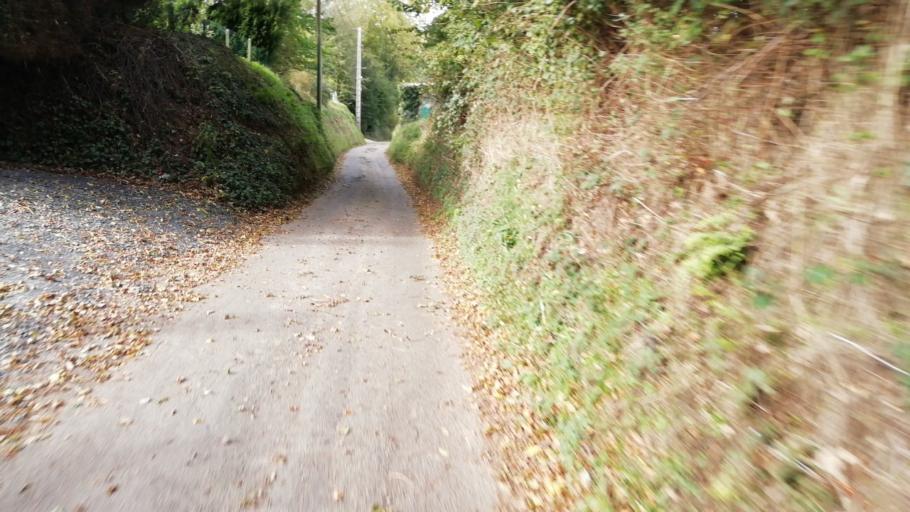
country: FR
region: Haute-Normandie
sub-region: Departement de la Seine-Maritime
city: Epouville
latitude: 49.5461
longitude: 0.2100
